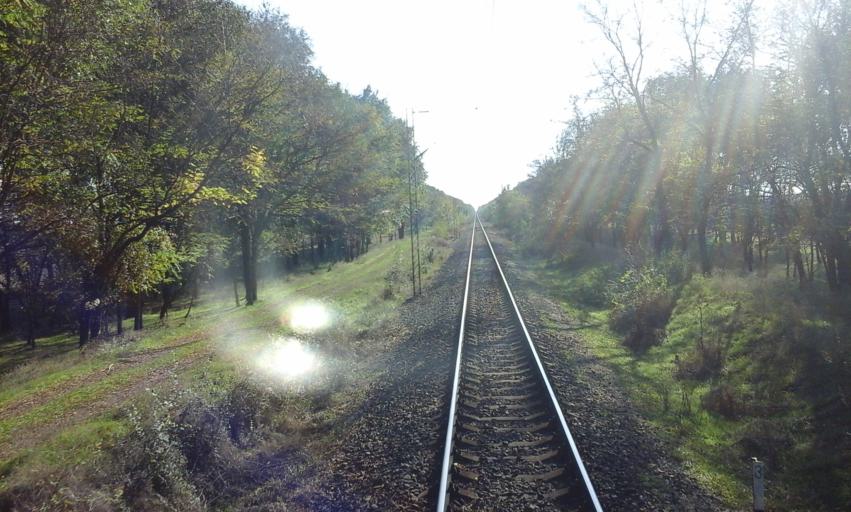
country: RS
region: Autonomna Pokrajina Vojvodina
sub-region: Severnobacki Okrug
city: Backa Topola
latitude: 45.8638
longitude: 19.6566
